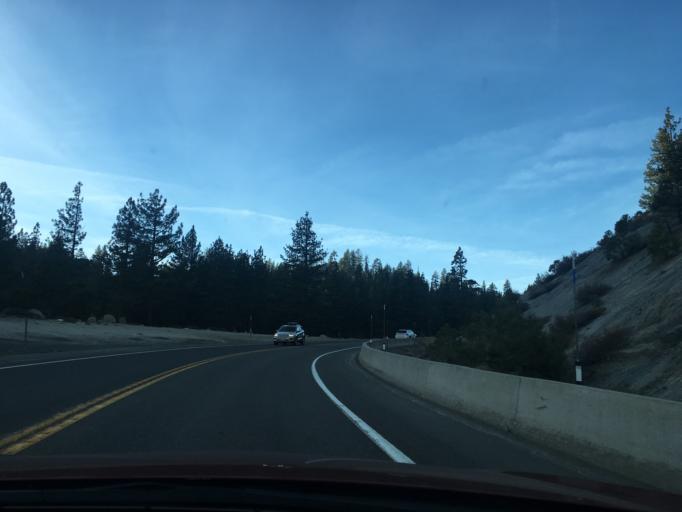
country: US
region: Nevada
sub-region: Douglas County
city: Kingsbury
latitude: 38.9762
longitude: -119.8831
